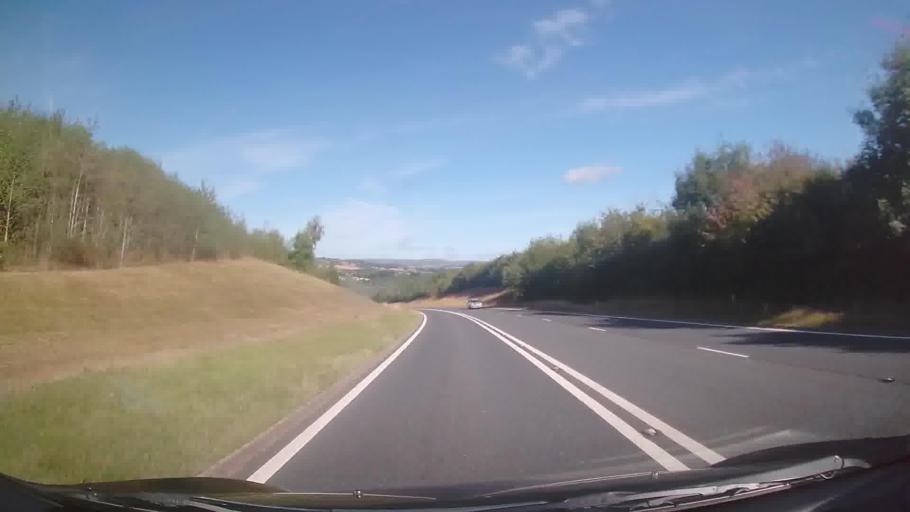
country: GB
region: Wales
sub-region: Sir Powys
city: Hay
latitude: 51.9898
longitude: -3.2335
